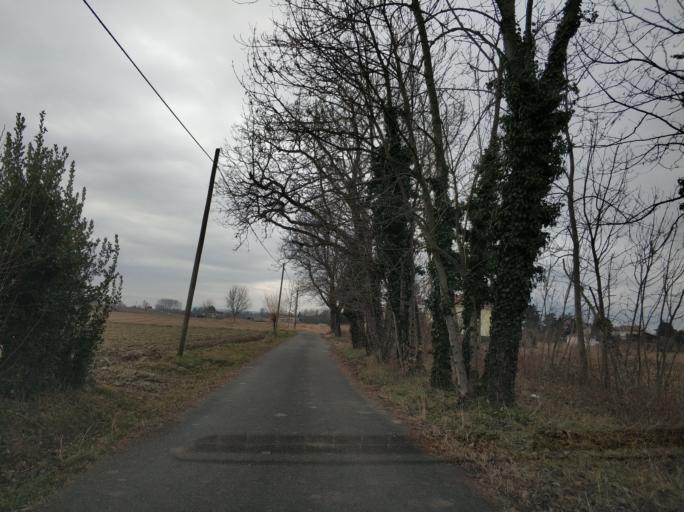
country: IT
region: Piedmont
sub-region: Provincia di Torino
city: Ivrea
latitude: 45.4453
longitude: 7.8831
